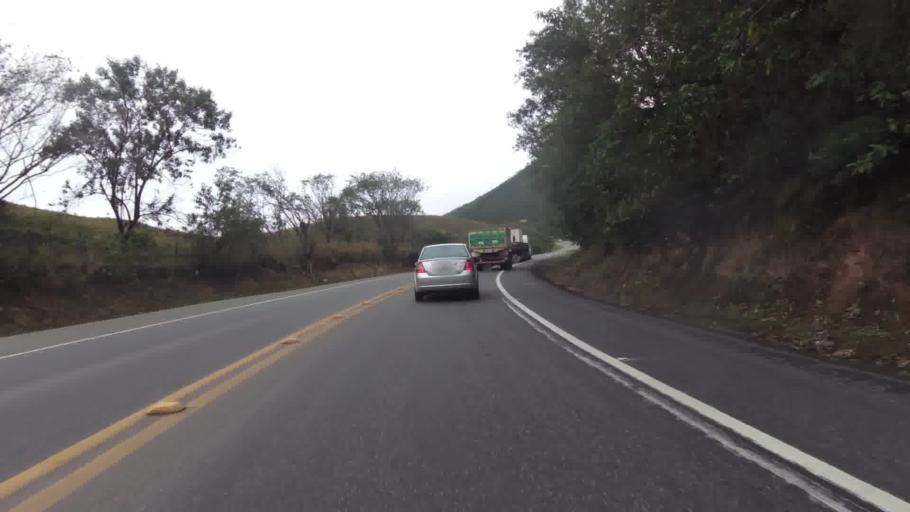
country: BR
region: Espirito Santo
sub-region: Rio Novo Do Sul
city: Rio Novo do Sul
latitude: -20.8646
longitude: -40.8820
